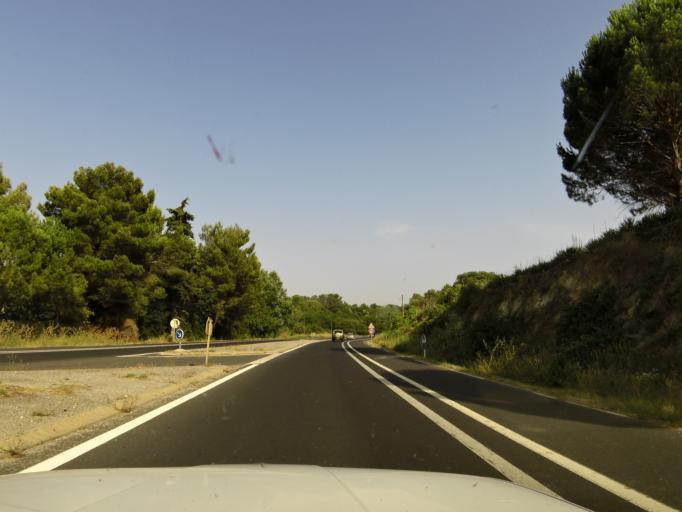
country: FR
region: Languedoc-Roussillon
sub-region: Departement de l'Herault
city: Clapiers
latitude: 43.6470
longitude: 3.8876
